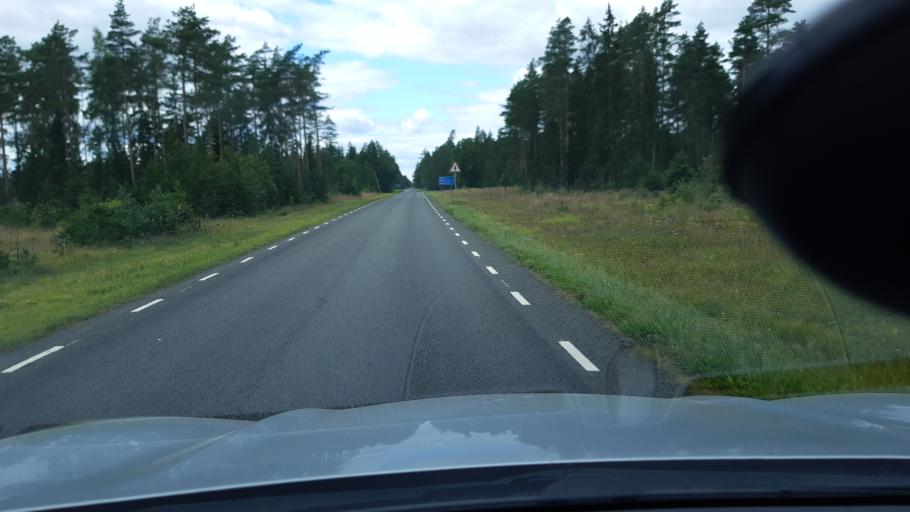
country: EE
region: Raplamaa
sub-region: Rapla vald
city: Rapla
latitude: 58.8964
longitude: 24.7009
